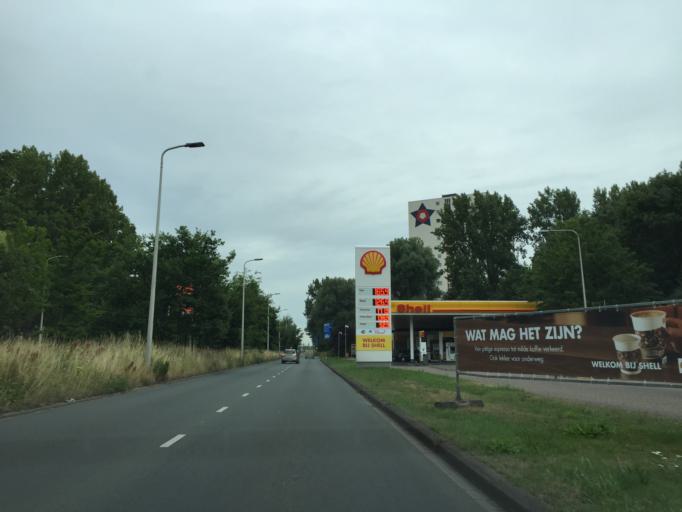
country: NL
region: South Holland
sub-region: Gemeente Westland
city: Kwintsheul
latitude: 52.0331
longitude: 4.2558
